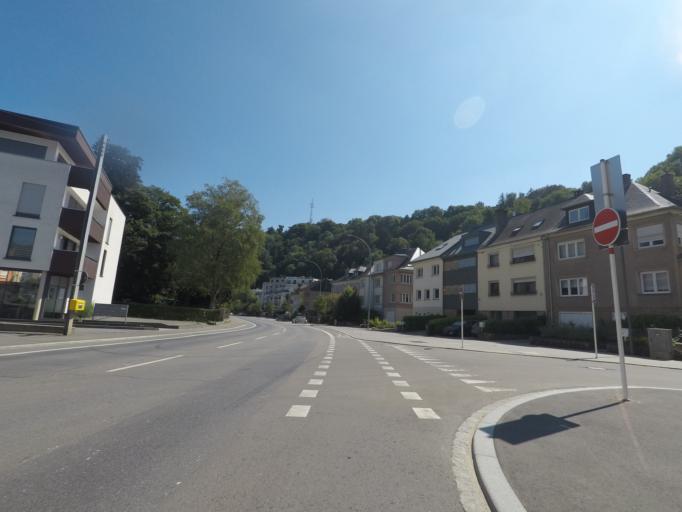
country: LU
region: Luxembourg
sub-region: Canton de Luxembourg
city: Luxembourg
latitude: 49.6277
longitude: 6.1225
